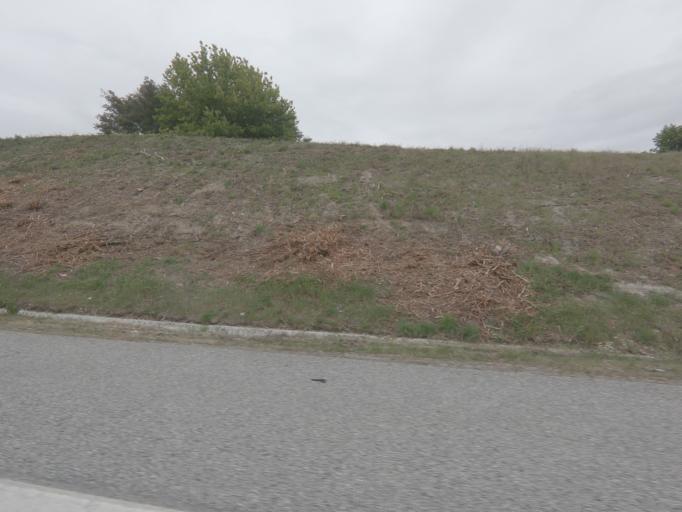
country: PT
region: Viseu
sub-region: Viseu
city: Rio de Loba
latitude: 40.6487
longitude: -7.8685
